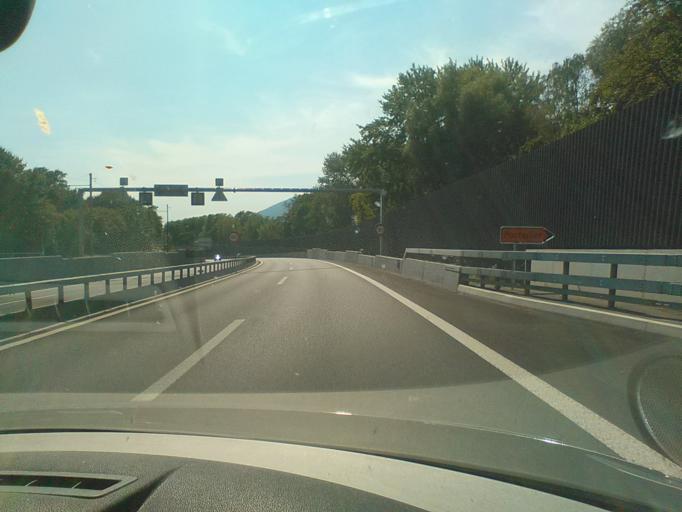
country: CH
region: Neuchatel
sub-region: Boudry District
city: Auvernier
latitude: 46.9775
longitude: 6.8845
